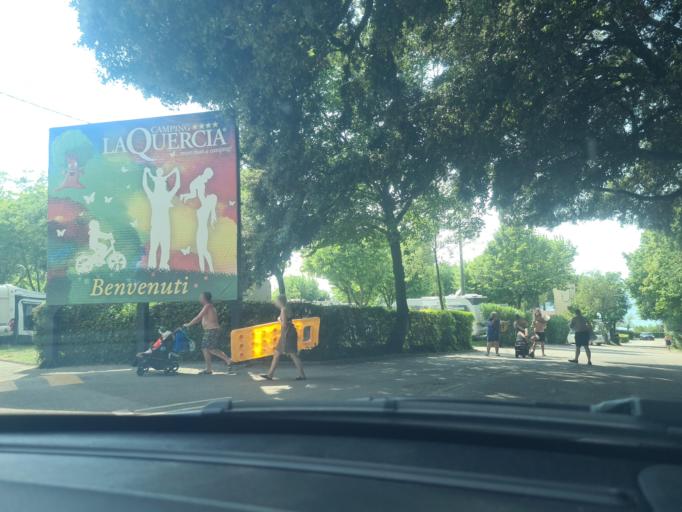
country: IT
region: Veneto
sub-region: Provincia di Verona
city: Lazise
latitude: 45.4934
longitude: 10.7327
